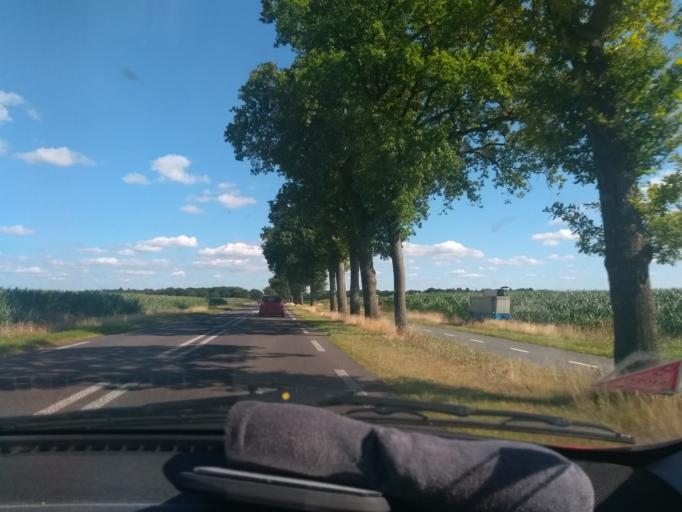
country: NL
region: Drenthe
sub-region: Gemeente Tynaarlo
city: Vries
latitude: 53.0918
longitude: 6.5537
